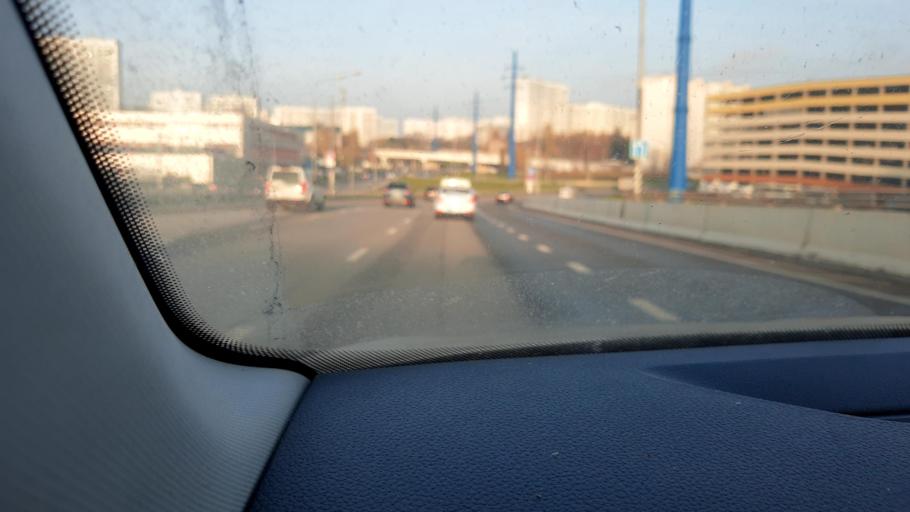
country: RU
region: Moskovskaya
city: Bol'shaya Setun'
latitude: 55.7073
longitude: 37.4099
